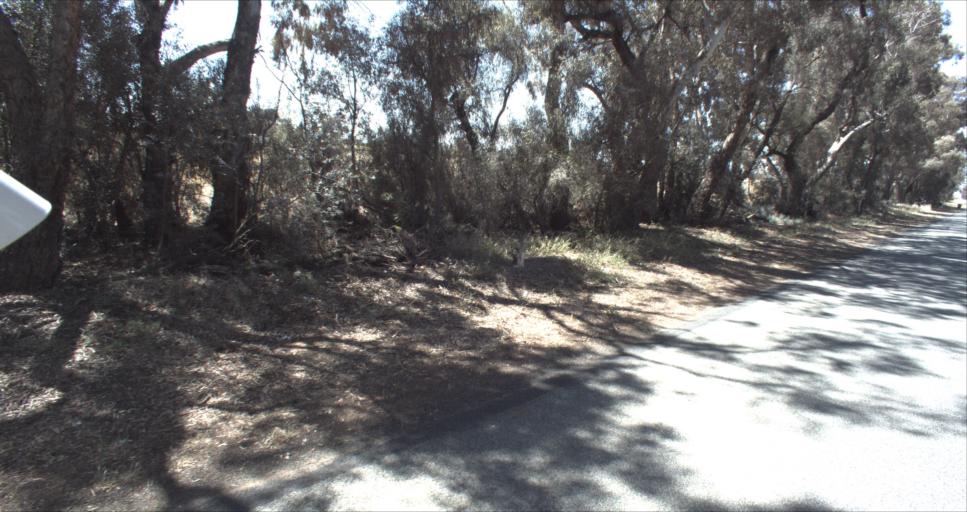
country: AU
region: New South Wales
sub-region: Leeton
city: Leeton
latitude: -34.5321
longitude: 146.3410
